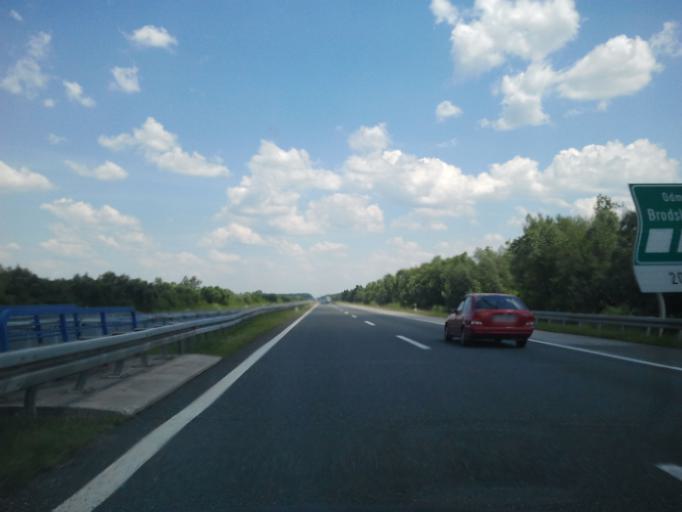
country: HR
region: Brodsko-Posavska
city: Oriovac
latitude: 45.1517
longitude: 17.7858
